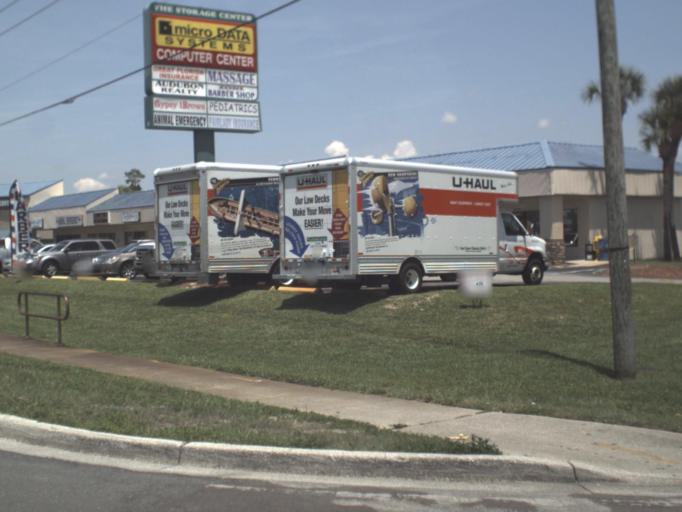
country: US
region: Florida
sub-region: Pasco County
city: Port Richey
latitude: 28.2843
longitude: -82.7149
